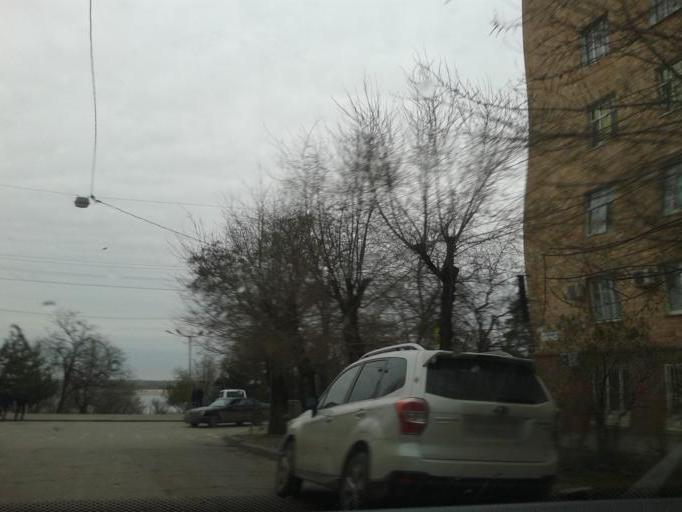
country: RU
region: Volgograd
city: Volgograd
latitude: 48.7113
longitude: 44.5293
